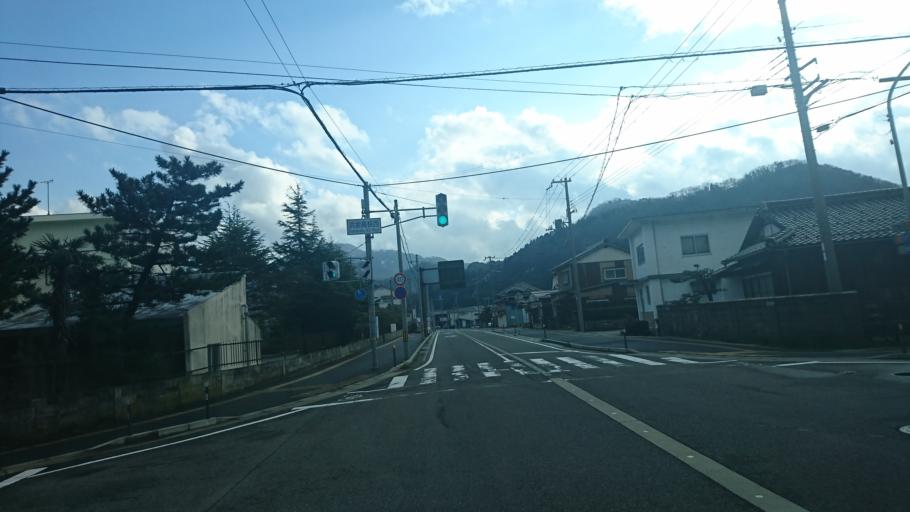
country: JP
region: Tottori
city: Tottori
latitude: 35.6272
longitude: 134.4454
